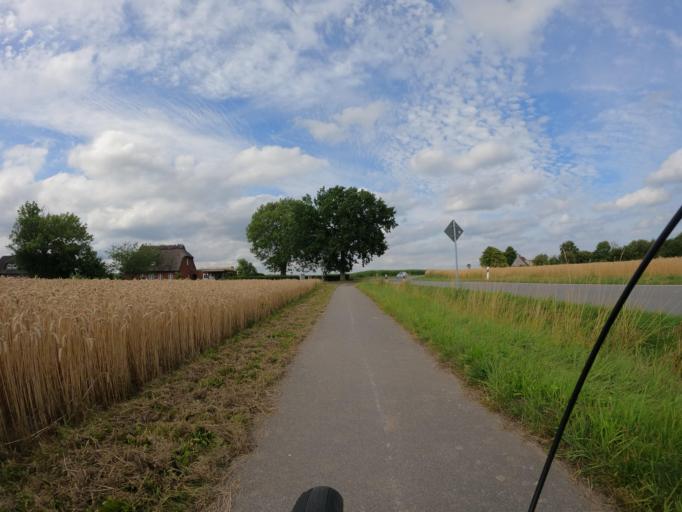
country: DE
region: Schleswig-Holstein
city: Steinberg
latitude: 54.7711
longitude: 9.7679
